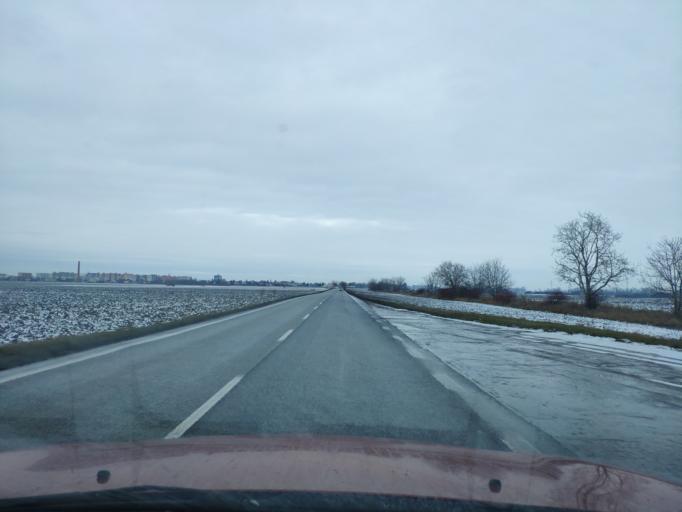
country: SK
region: Nitriansky
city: Sellye
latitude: 48.1581
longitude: 17.9107
